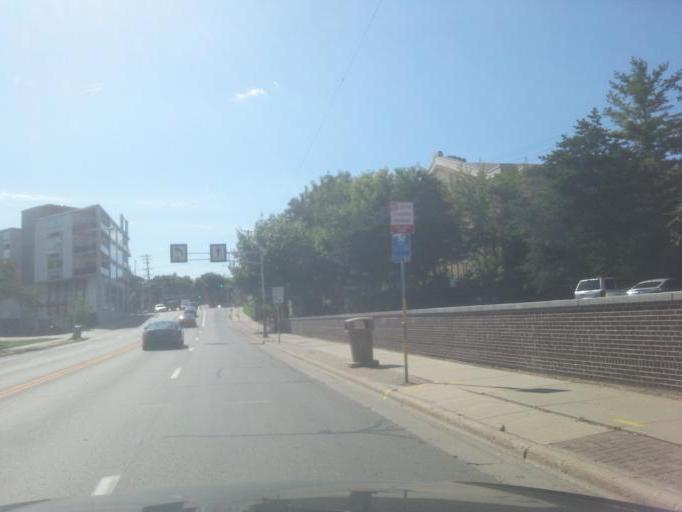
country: US
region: Wisconsin
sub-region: Dane County
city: Madison
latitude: 43.0679
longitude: -89.4112
